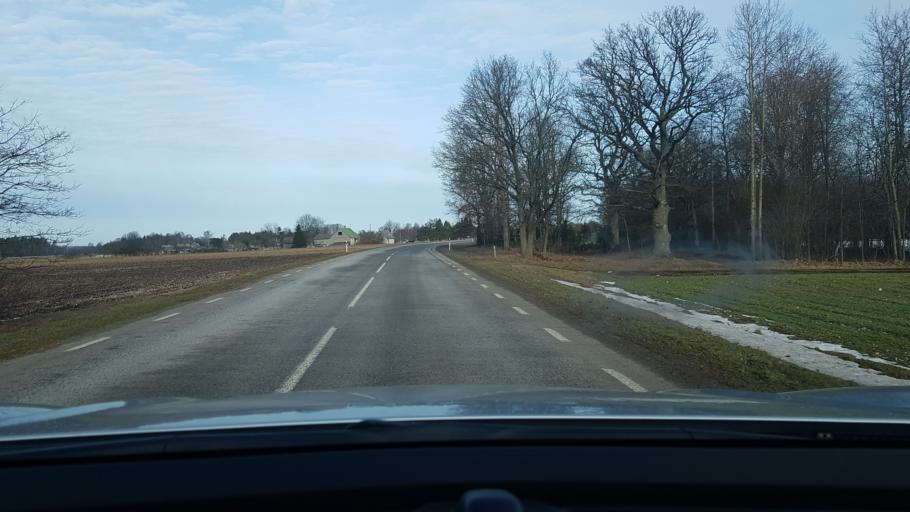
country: EE
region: Saare
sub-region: Kuressaare linn
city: Kuressaare
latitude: 58.5003
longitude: 22.7055
